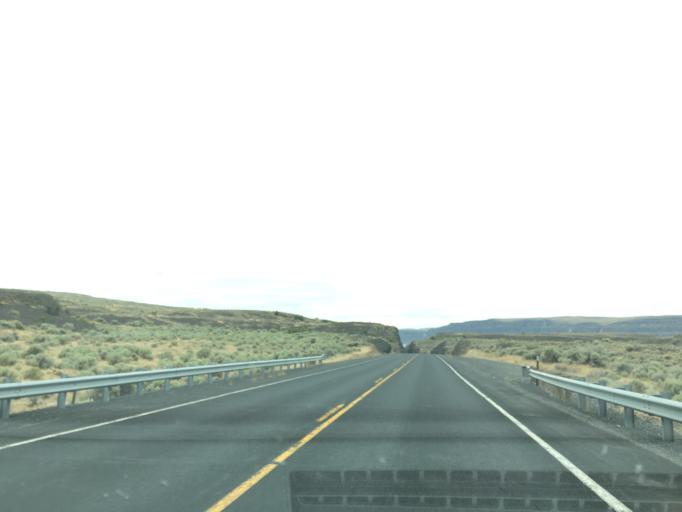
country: US
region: Washington
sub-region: Okanogan County
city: Coulee Dam
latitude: 47.7307
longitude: -119.2463
